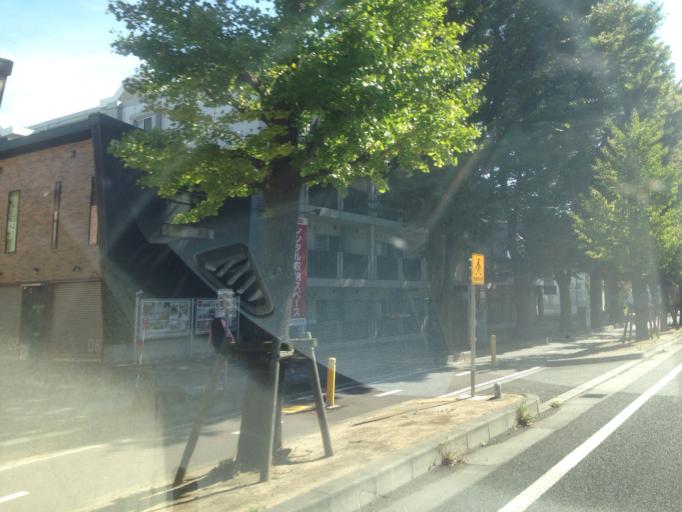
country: JP
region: Tokyo
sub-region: Machida-shi
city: Machida
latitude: 35.5742
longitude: 139.3714
